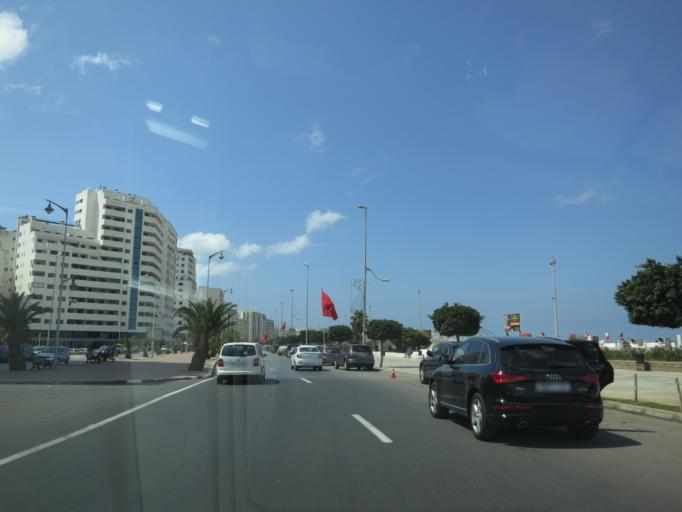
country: MA
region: Tanger-Tetouan
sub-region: Tanger-Assilah
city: Tangier
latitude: 35.7759
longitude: -5.7939
